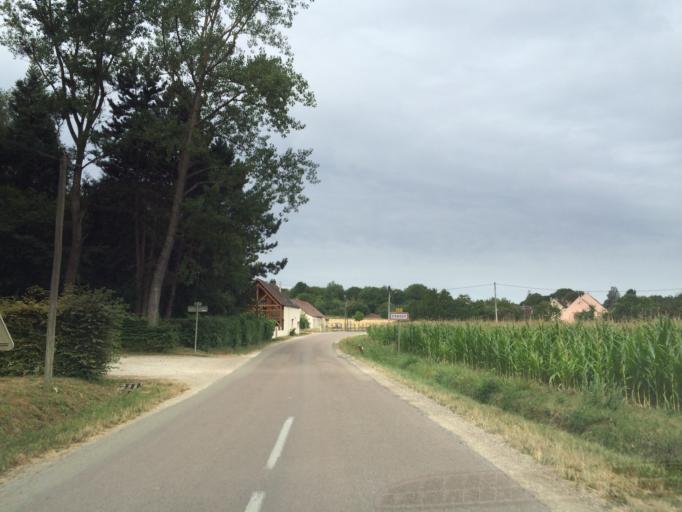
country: FR
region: Bourgogne
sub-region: Departement de l'Yonne
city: Aillant-sur-Tholon
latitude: 47.8522
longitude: 3.3546
